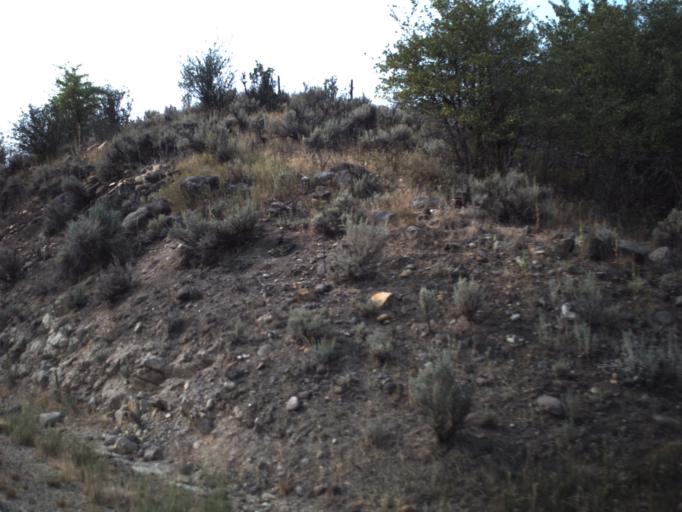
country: US
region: Utah
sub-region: Morgan County
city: Morgan
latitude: 40.9787
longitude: -111.5376
